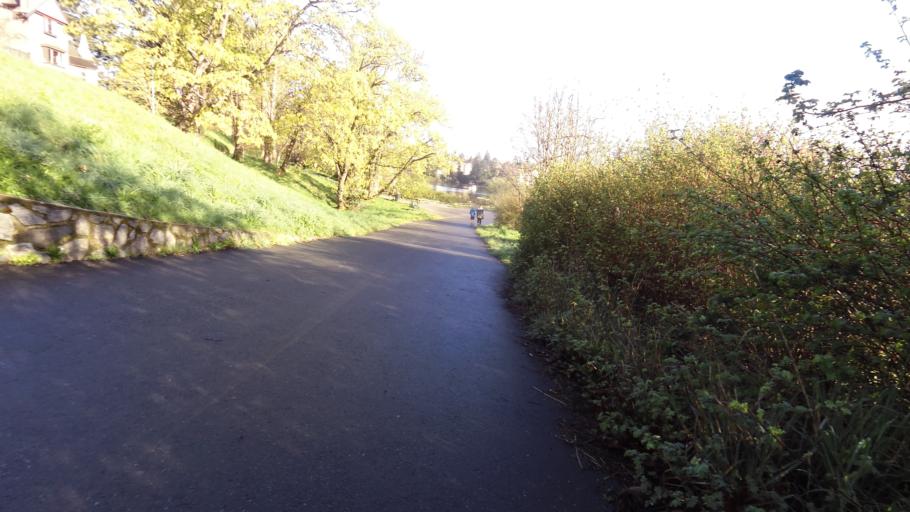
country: CA
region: British Columbia
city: Victoria
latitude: 48.4373
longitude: -123.3832
